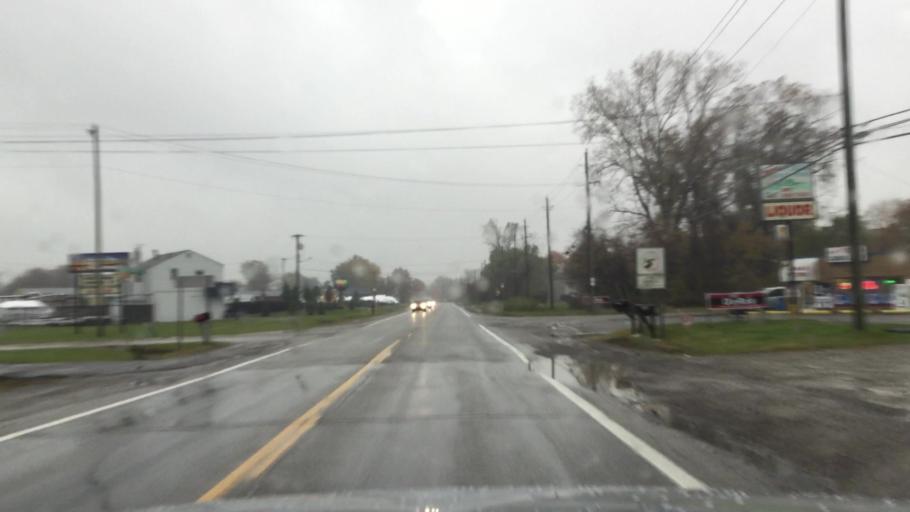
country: US
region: Michigan
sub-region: Macomb County
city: New Baltimore
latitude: 42.6577
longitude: -82.7832
